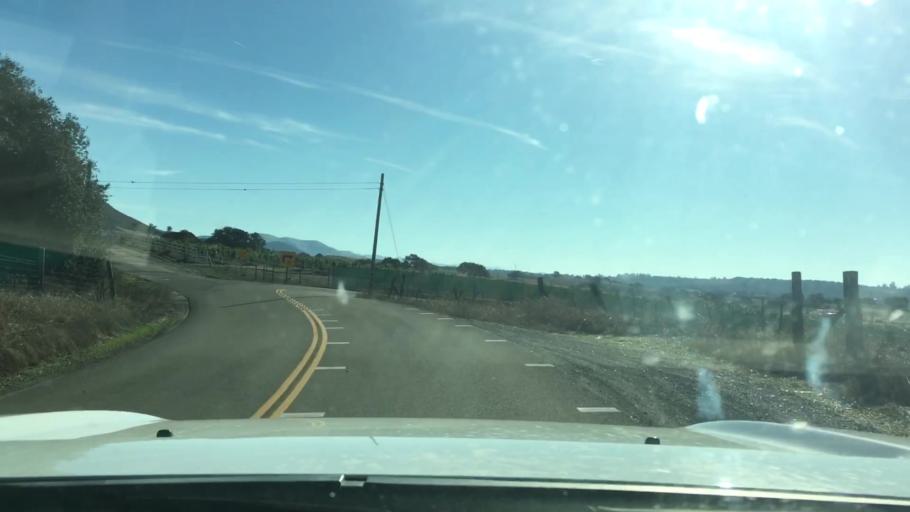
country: US
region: California
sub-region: San Luis Obispo County
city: Arroyo Grande
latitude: 35.1048
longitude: -120.5586
